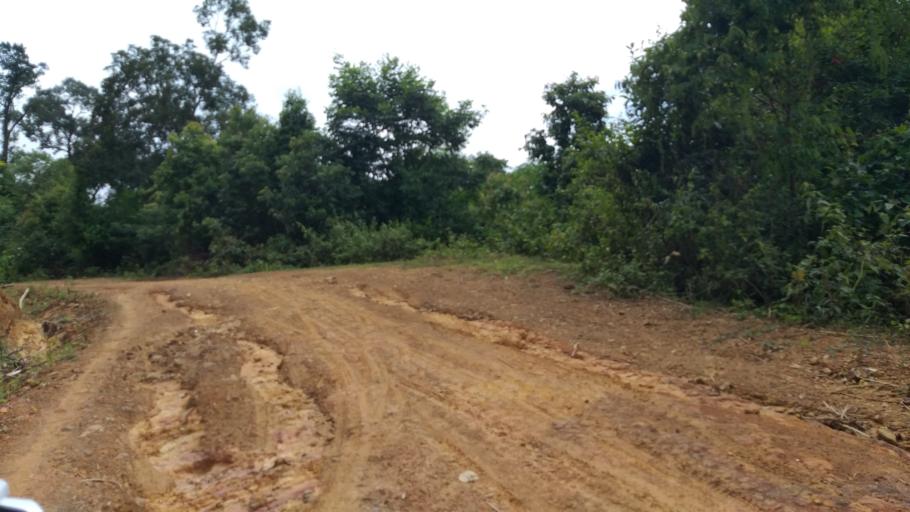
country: LA
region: Phongsali
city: Khoa
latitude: 21.3882
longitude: 102.6593
